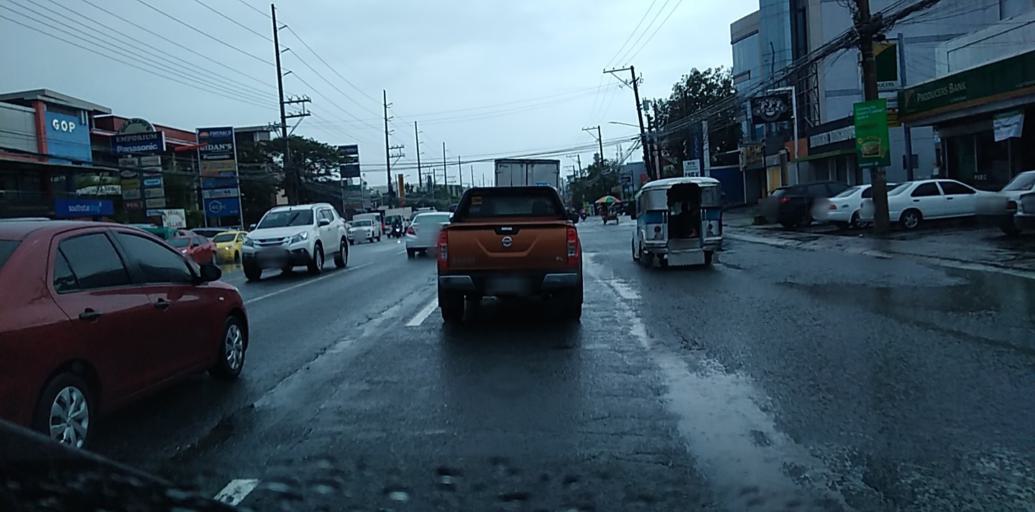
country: PH
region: Central Luzon
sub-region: Province of Pampanga
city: Magliman
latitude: 15.0433
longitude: 120.6748
